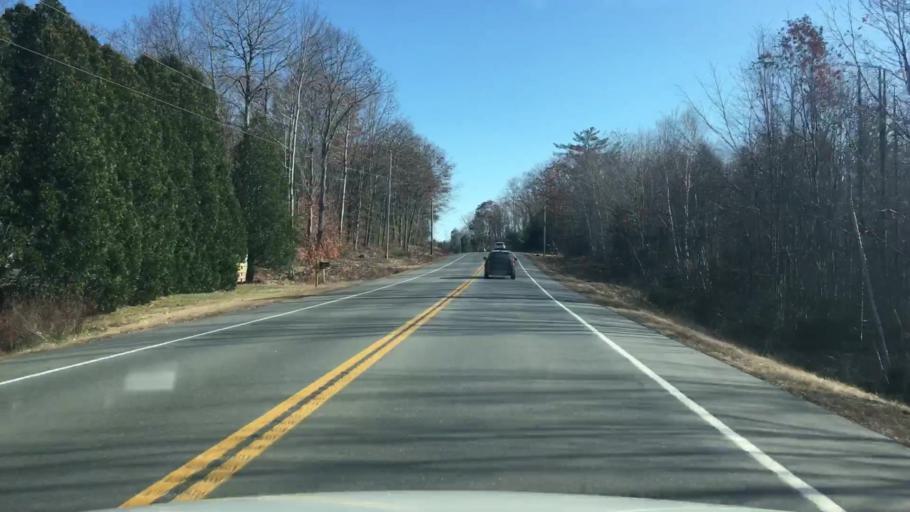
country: US
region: Maine
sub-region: Knox County
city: Washington
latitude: 44.2499
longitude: -69.4062
